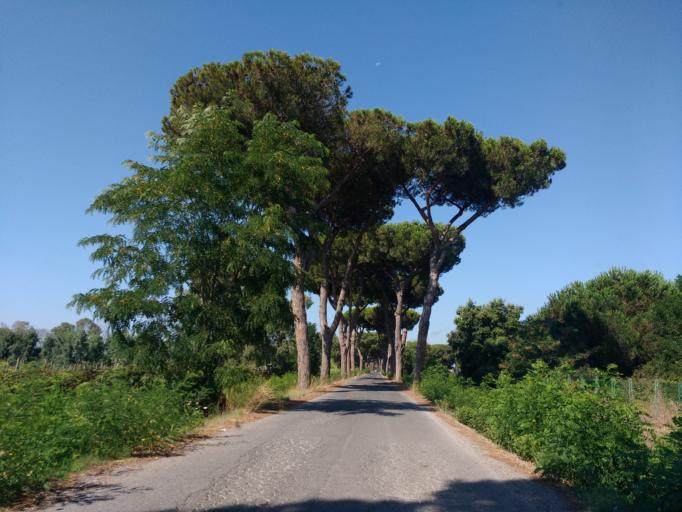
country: IT
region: Latium
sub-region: Citta metropolitana di Roma Capitale
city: Acilia-Castel Fusano-Ostia Antica
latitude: 41.7551
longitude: 12.3429
